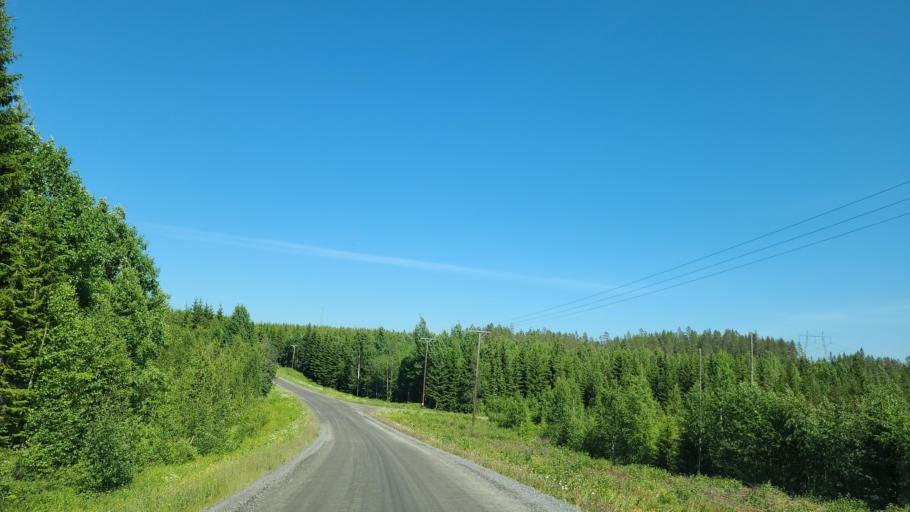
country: SE
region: Vaesterbotten
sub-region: Bjurholms Kommun
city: Bjurholm
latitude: 63.6399
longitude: 19.2072
